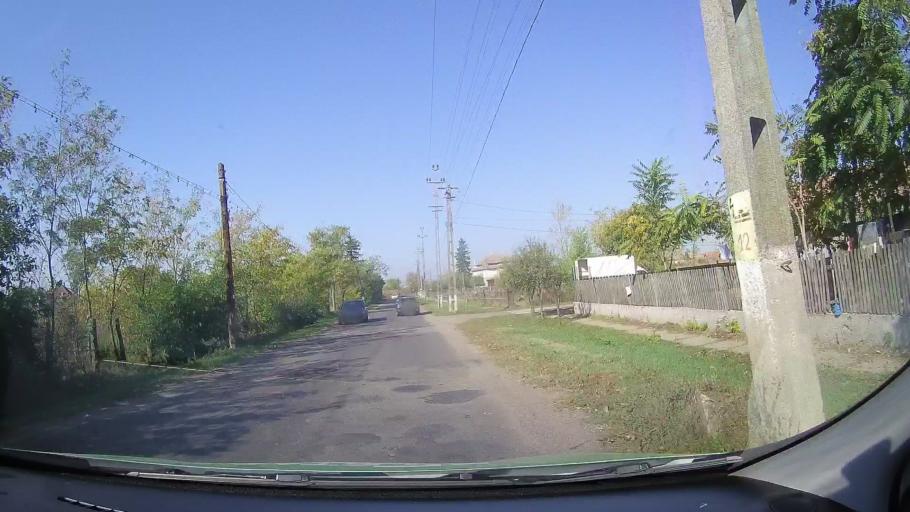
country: RO
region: Satu Mare
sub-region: Comuna Sanislau
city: Sanislau
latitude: 47.6331
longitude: 22.3286
